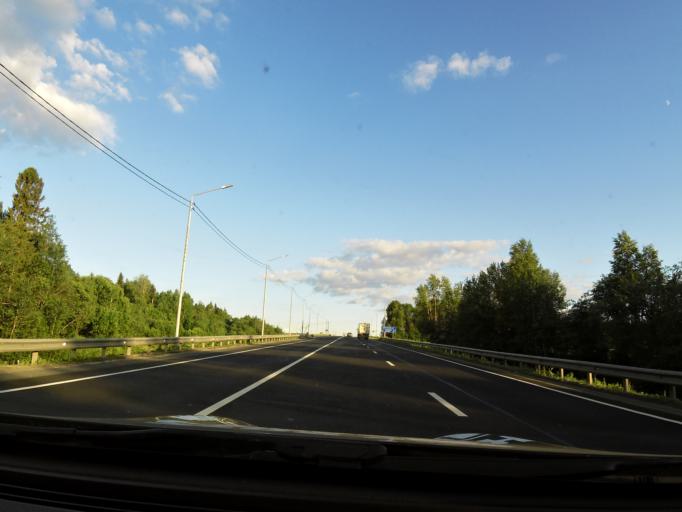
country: RU
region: Vologda
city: Gryazovets
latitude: 59.0243
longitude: 40.1142
